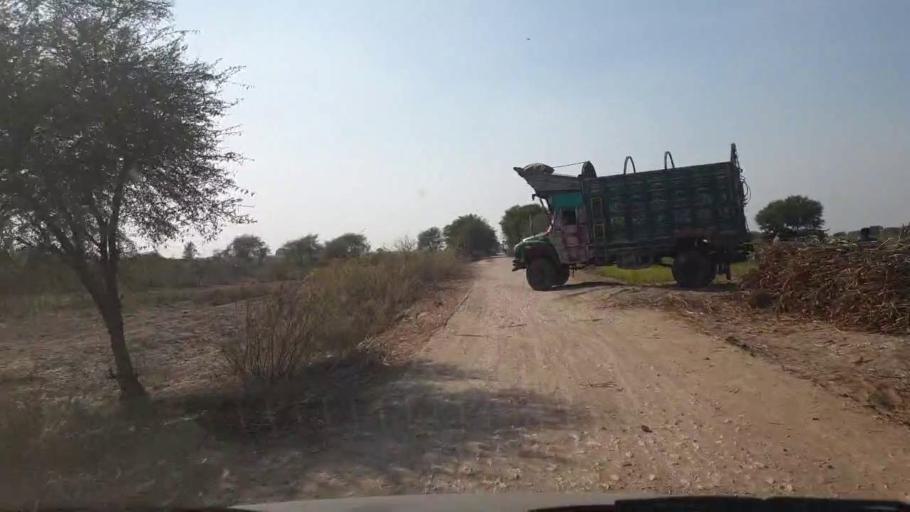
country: PK
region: Sindh
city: Chambar
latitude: 25.3175
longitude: 68.7653
